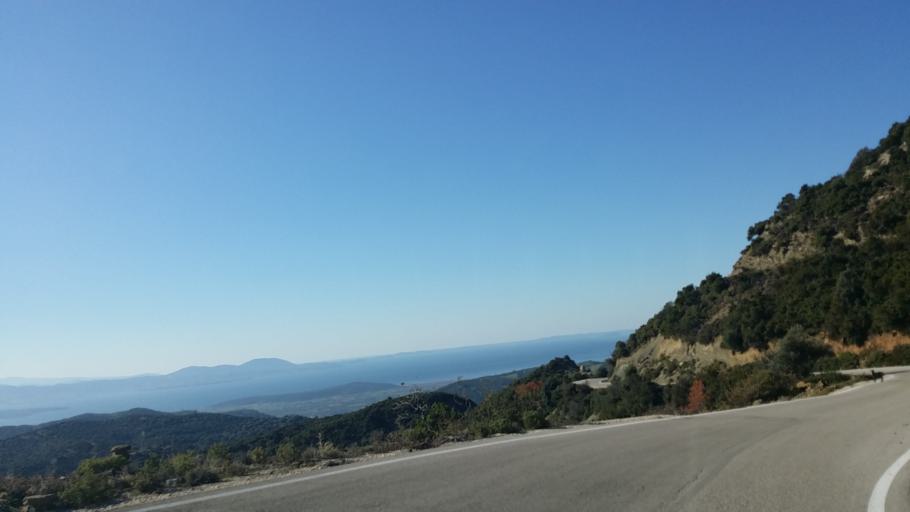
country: GR
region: West Greece
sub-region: Nomos Aitolias kai Akarnanias
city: Krikellos
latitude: 38.9544
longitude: 21.2431
